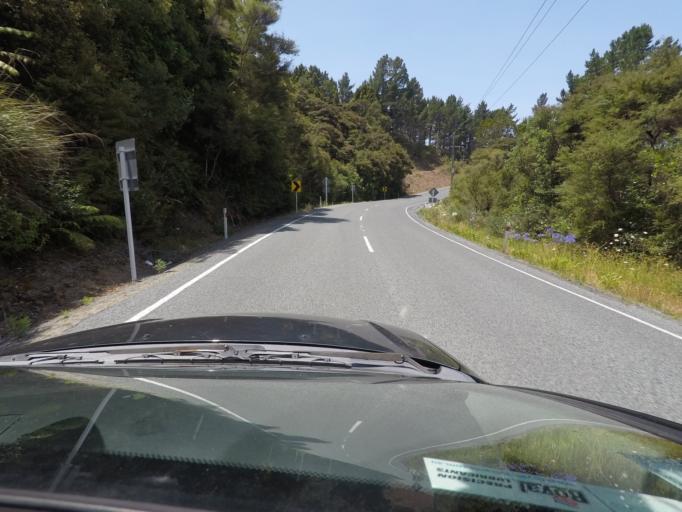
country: NZ
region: Auckland
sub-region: Auckland
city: Warkworth
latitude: -36.3173
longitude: 174.7438
